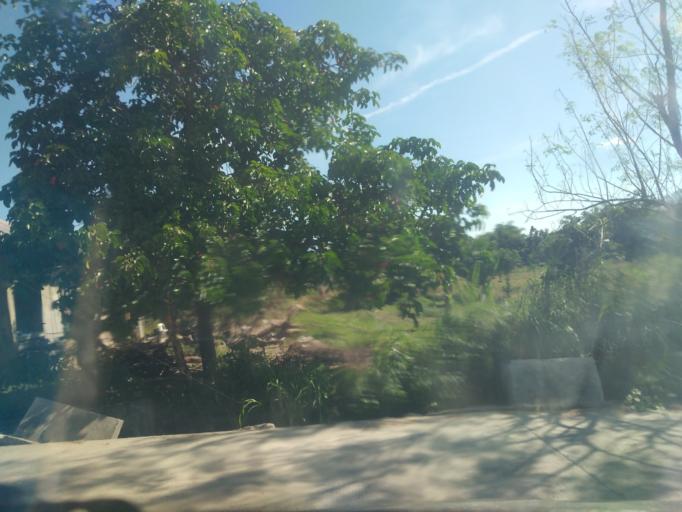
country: PH
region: Central Luzon
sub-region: Province of Pampanga
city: Calibutbut
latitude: 15.0941
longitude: 120.5923
